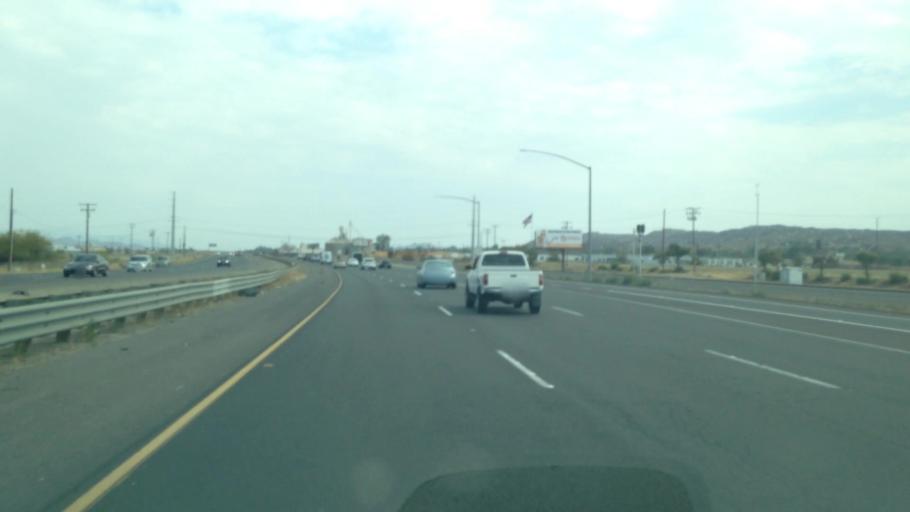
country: US
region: California
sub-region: Riverside County
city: Mead Valley
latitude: 33.8410
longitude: -117.2501
